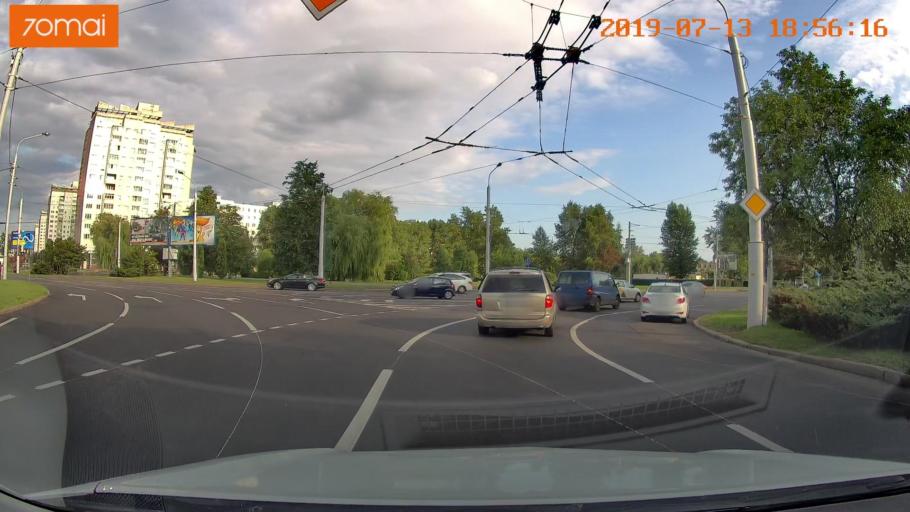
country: BY
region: Minsk
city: Minsk
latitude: 53.8785
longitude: 27.6091
